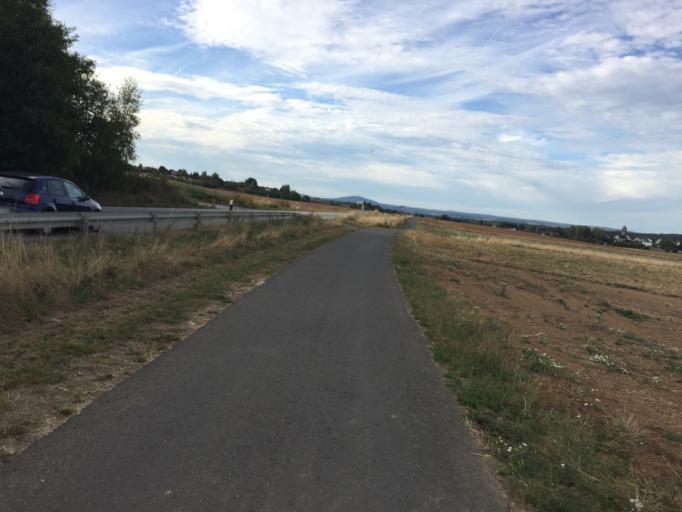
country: DE
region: Hesse
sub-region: Regierungsbezirk Giessen
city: Langgons
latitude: 50.5240
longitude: 8.7185
